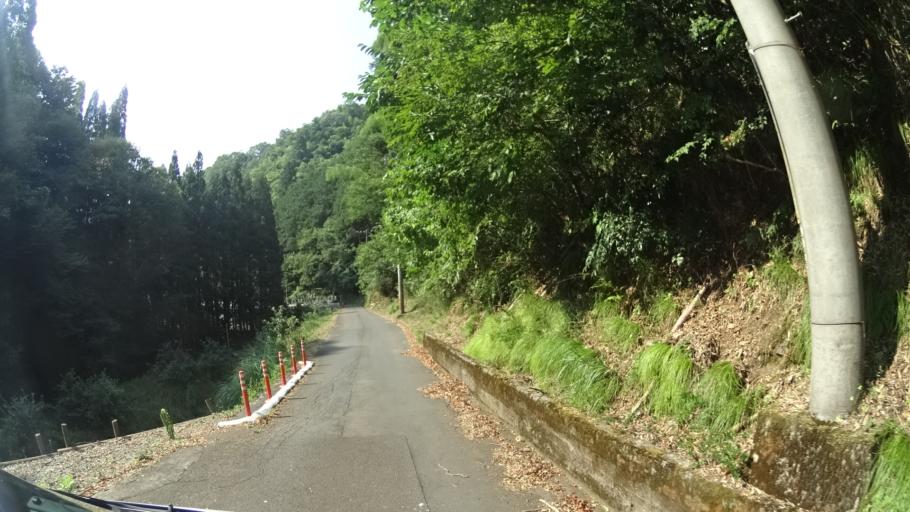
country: JP
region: Kyoto
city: Maizuru
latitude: 35.4079
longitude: 135.2342
